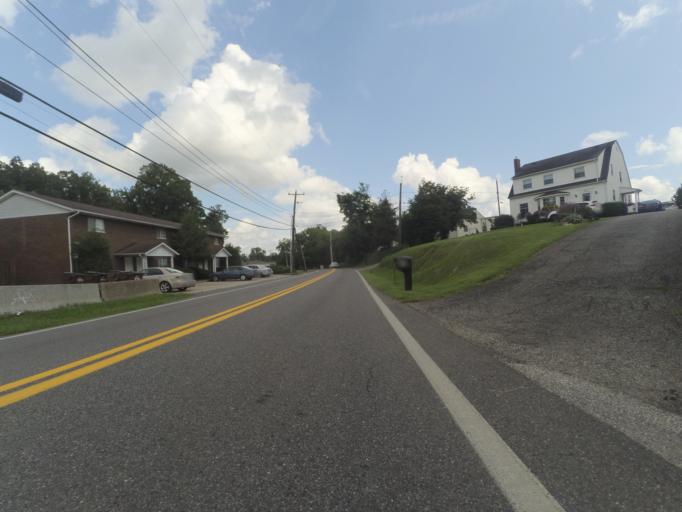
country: US
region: West Virginia
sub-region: Cabell County
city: Pea Ridge
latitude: 38.4163
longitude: -82.3161
